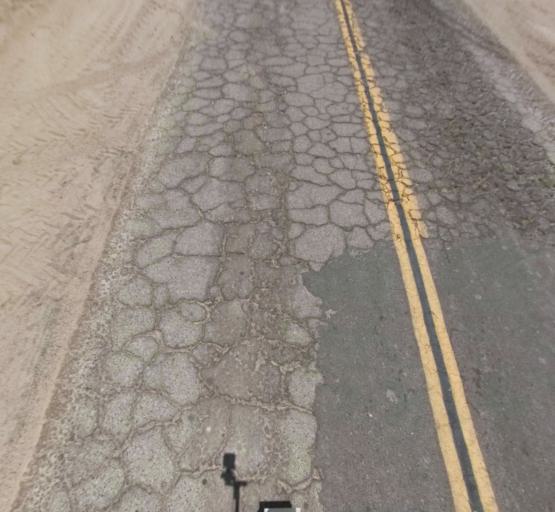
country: US
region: California
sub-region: Fresno County
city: Biola
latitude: 36.8298
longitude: -120.1510
